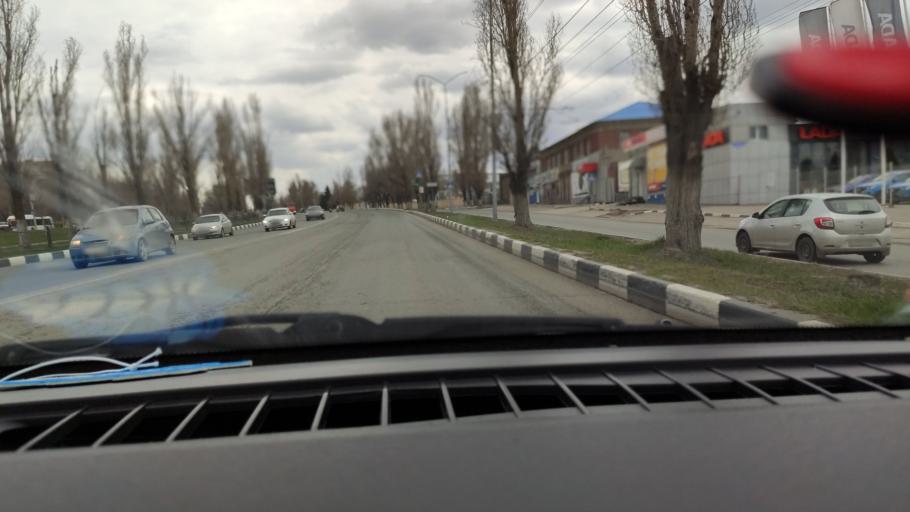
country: RU
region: Saratov
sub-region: Saratovskiy Rayon
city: Saratov
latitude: 51.6088
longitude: 45.9693
